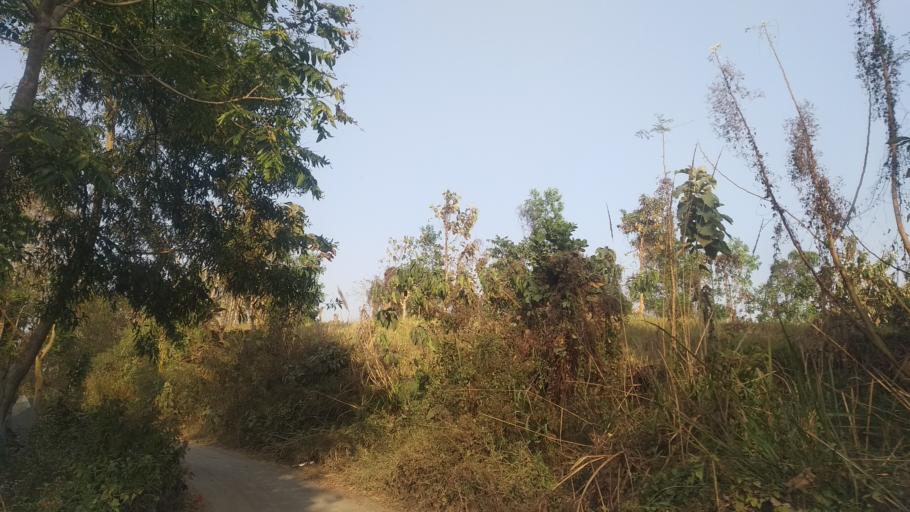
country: IN
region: Tripura
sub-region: West Tripura
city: Sonamura
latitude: 23.4350
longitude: 91.3573
